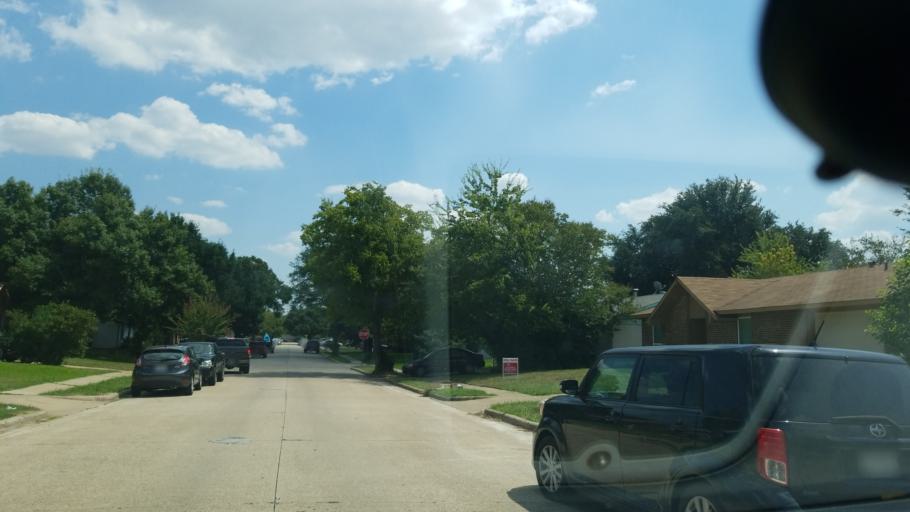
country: US
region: Texas
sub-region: Dallas County
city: Grand Prairie
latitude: 32.7047
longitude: -96.9914
